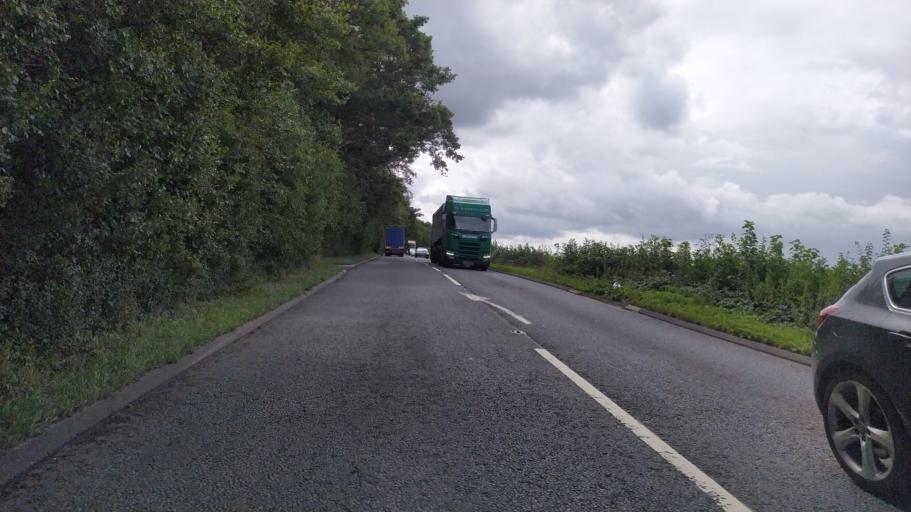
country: GB
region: England
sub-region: Wiltshire
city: North Bradley
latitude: 51.3065
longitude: -2.1734
